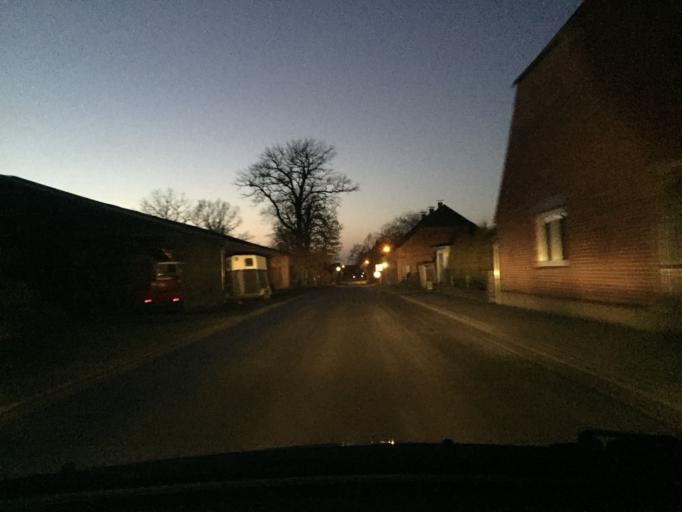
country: DE
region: Lower Saxony
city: Nahrendorf
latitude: 53.1729
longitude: 10.8151
